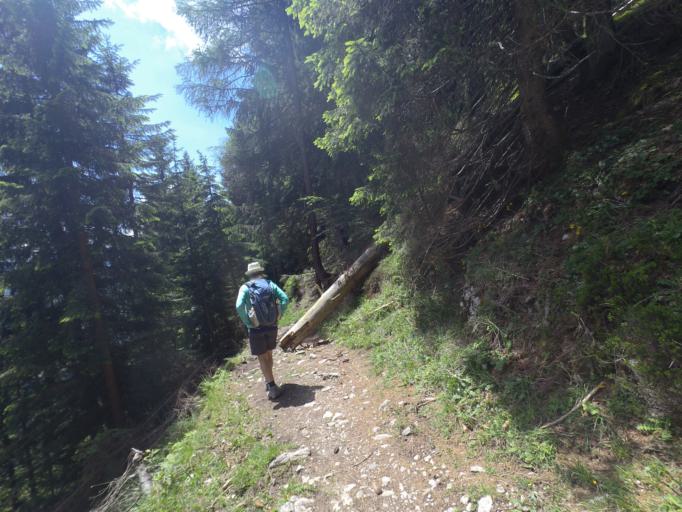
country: AT
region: Salzburg
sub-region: Politischer Bezirk Zell am See
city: Leogang
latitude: 47.4635
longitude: 12.7741
